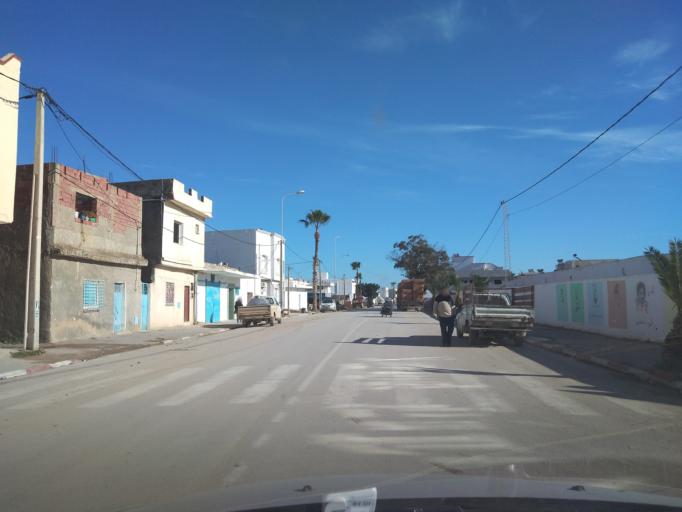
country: TN
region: Ariana
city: Qal'at al Andalus
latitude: 37.0624
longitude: 10.1203
